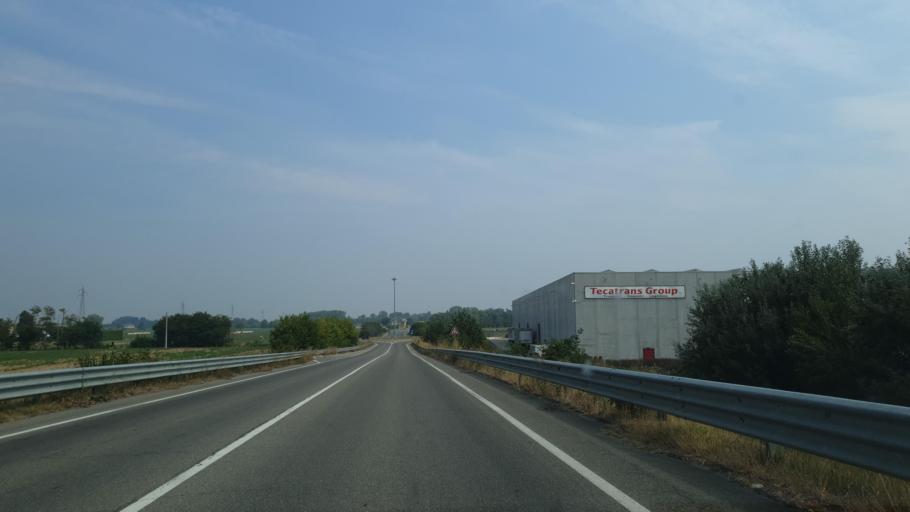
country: IT
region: Emilia-Romagna
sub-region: Provincia di Parma
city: San Secondo Parmense
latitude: 44.9284
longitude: 10.2333
